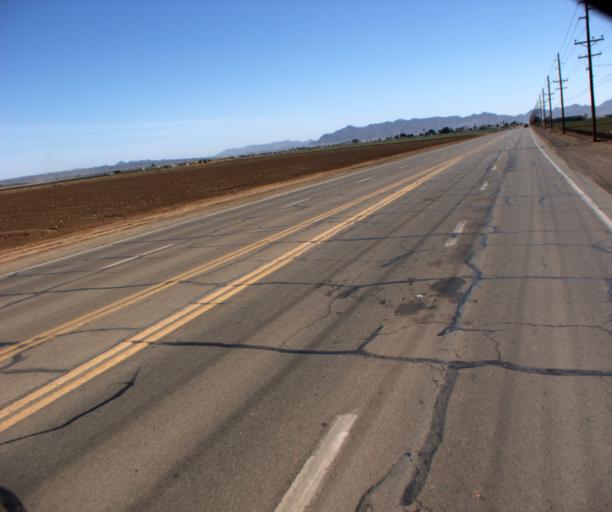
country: US
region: Arizona
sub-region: Yuma County
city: Yuma
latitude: 32.6990
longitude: -114.5438
